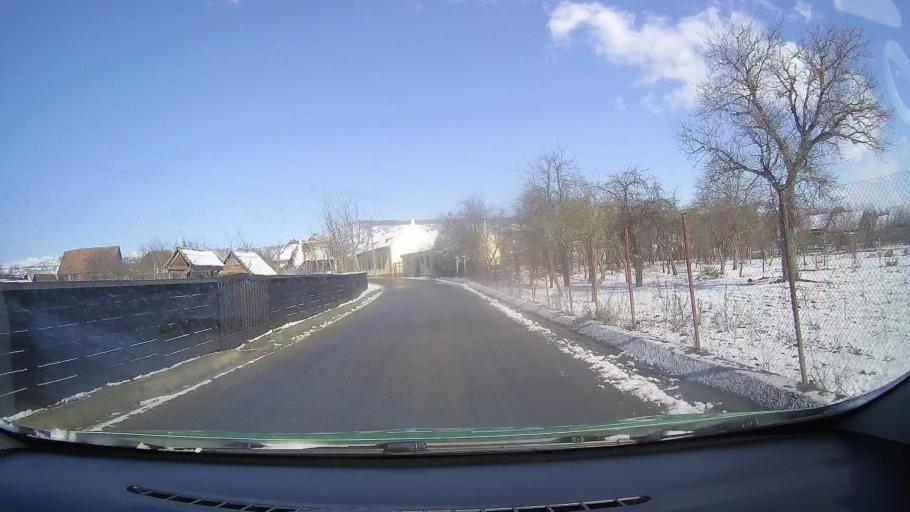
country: RO
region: Sibiu
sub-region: Comuna Avrig
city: Avrig
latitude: 45.7599
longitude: 24.3898
